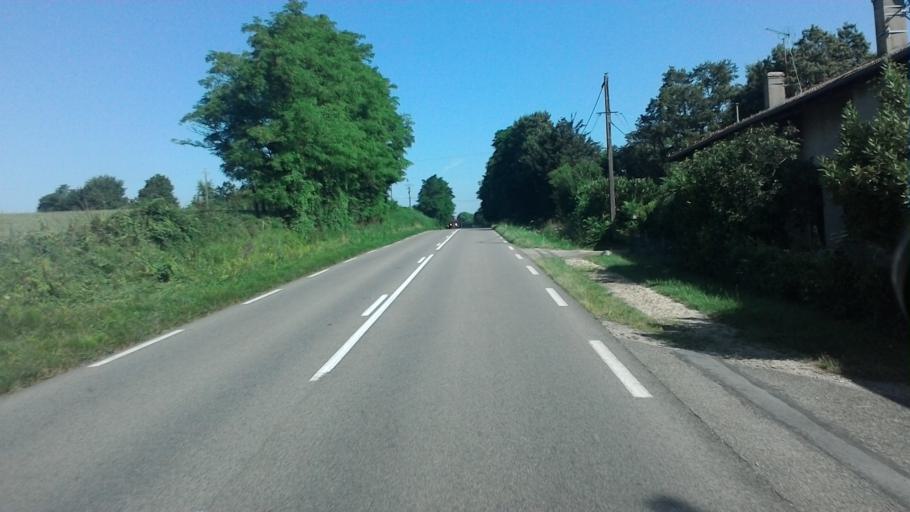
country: FR
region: Rhone-Alpes
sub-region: Departement de l'Ain
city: Saint-Trivier-de-Courtes
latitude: 46.4291
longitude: 5.0967
